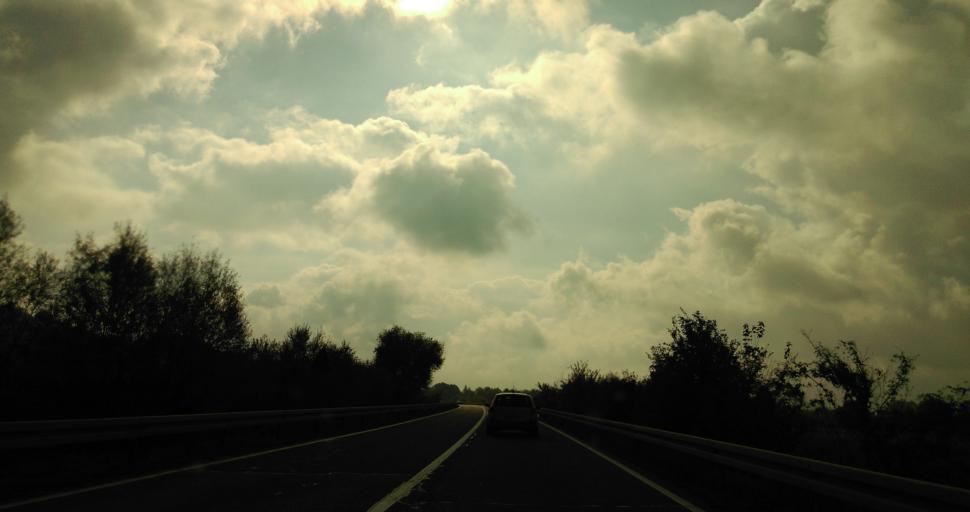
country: RS
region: Central Serbia
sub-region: Kolubarski Okrug
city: Ljig
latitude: 44.2931
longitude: 20.2639
